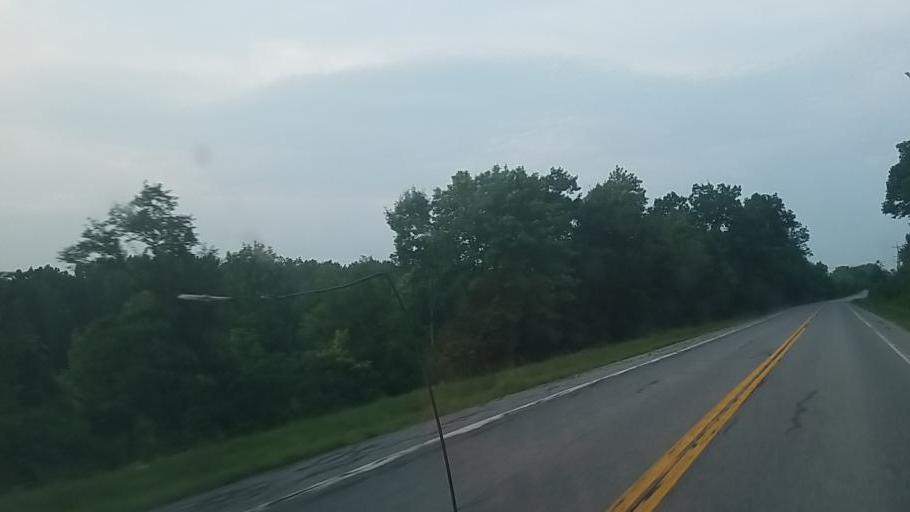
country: US
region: New York
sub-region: Montgomery County
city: Fonda
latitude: 42.9329
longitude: -74.4120
